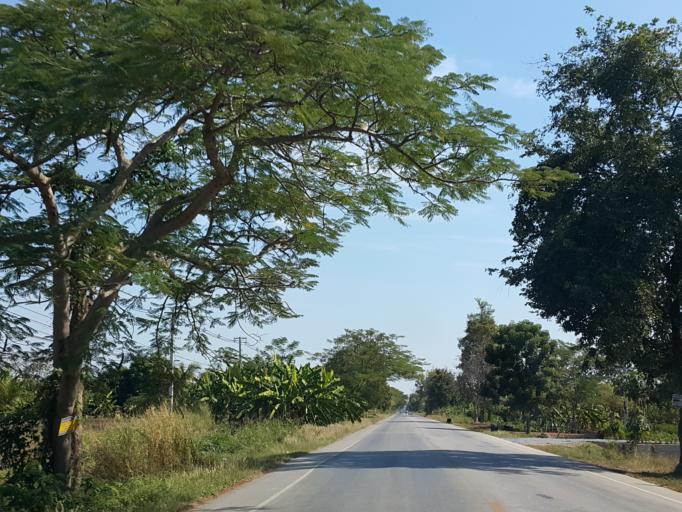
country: TH
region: Sukhothai
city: Thung Saliam
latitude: 17.3169
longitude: 99.6575
